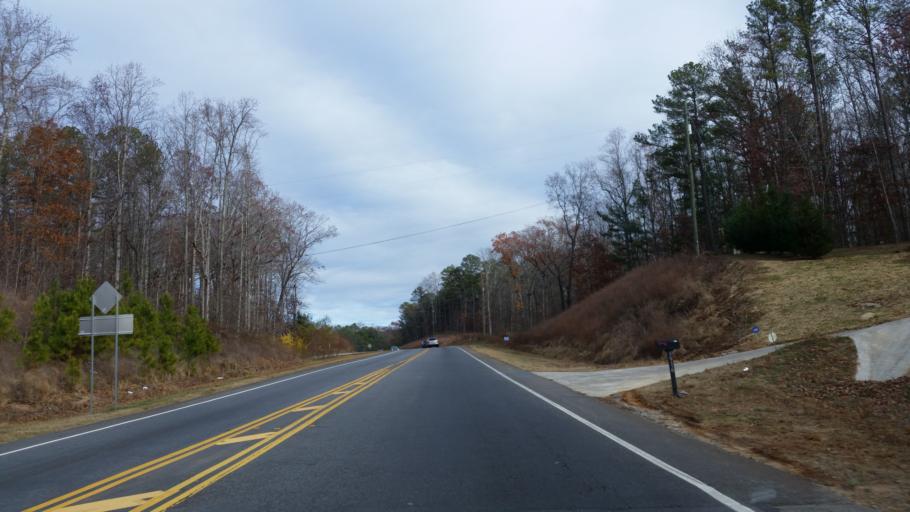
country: US
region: Georgia
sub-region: Bartow County
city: Cartersville
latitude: 34.2204
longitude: -84.7186
